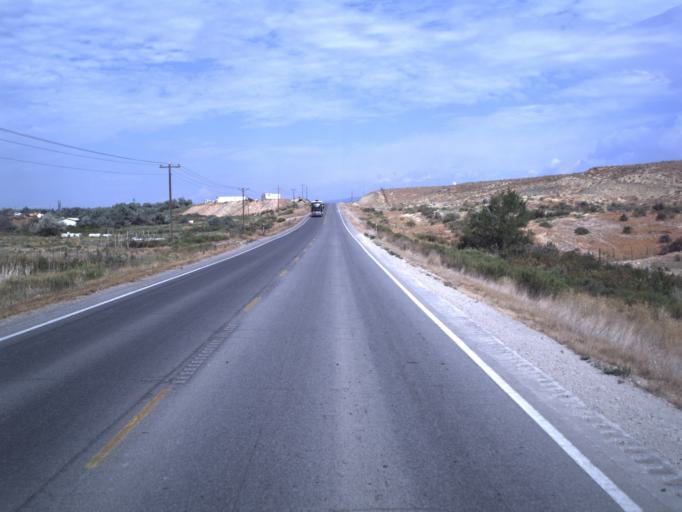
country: US
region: Utah
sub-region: Uintah County
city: Naples
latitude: 40.3931
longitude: -109.4498
